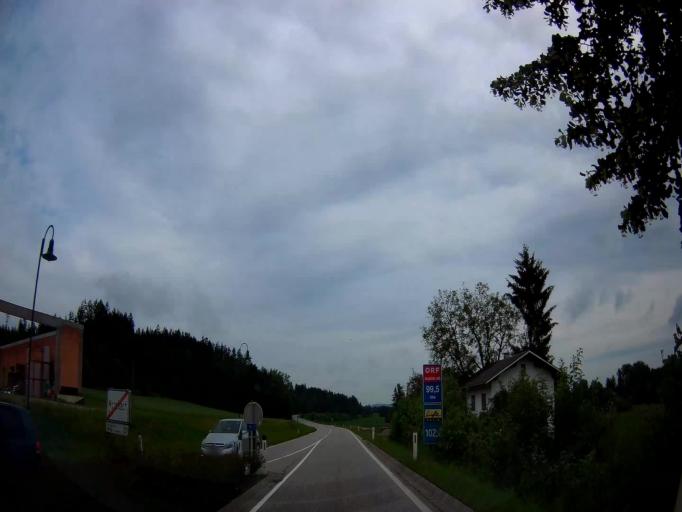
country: AT
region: Upper Austria
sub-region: Politischer Bezirk Braunau am Inn
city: Altheim
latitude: 48.2103
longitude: 13.1644
